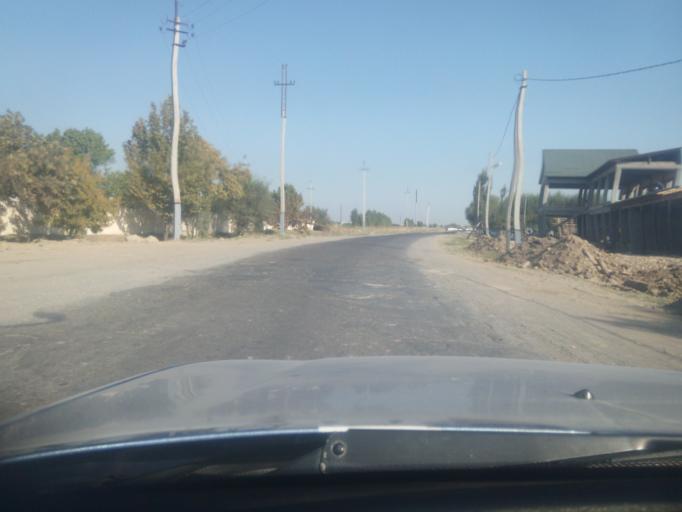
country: UZ
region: Sirdaryo
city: Guliston
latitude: 40.4961
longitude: 68.8001
